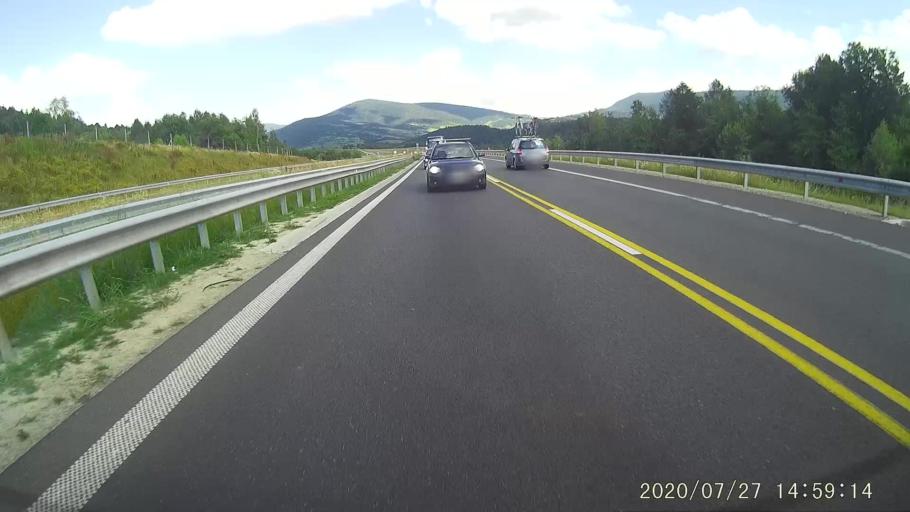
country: PL
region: Lesser Poland Voivodeship
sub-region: Powiat myslenicki
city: Krzczonow
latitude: 49.6948
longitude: 19.9173
